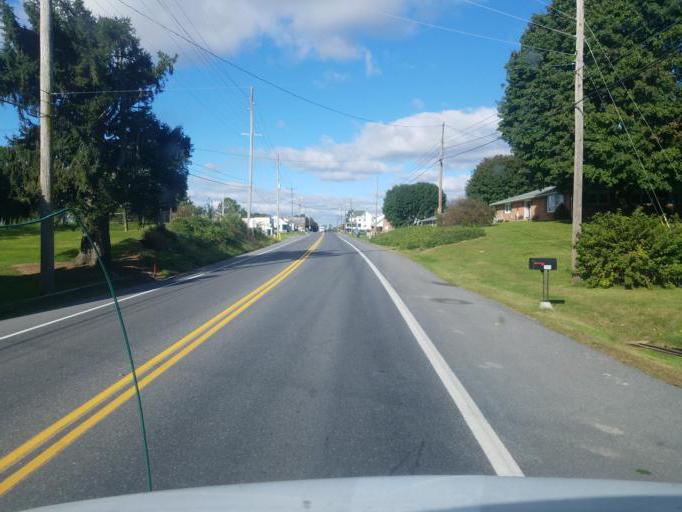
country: US
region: Pennsylvania
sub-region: Franklin County
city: Greencastle
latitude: 39.7769
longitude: -77.6653
